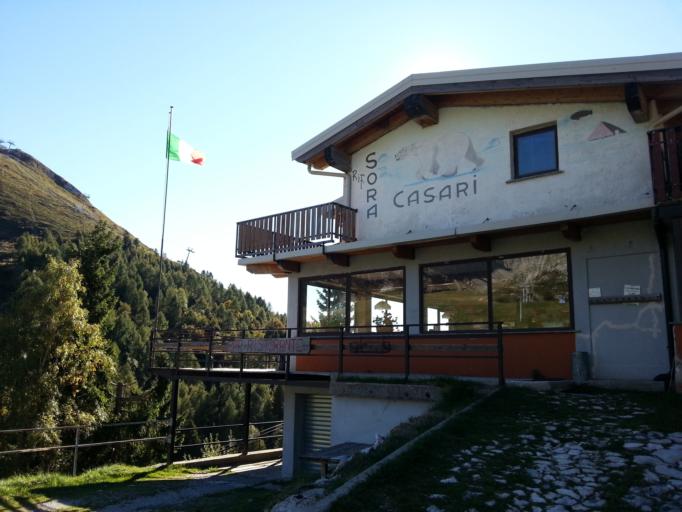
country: IT
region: Lombardy
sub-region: Provincia di Lecco
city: Moggio
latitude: 45.9600
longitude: 9.4936
